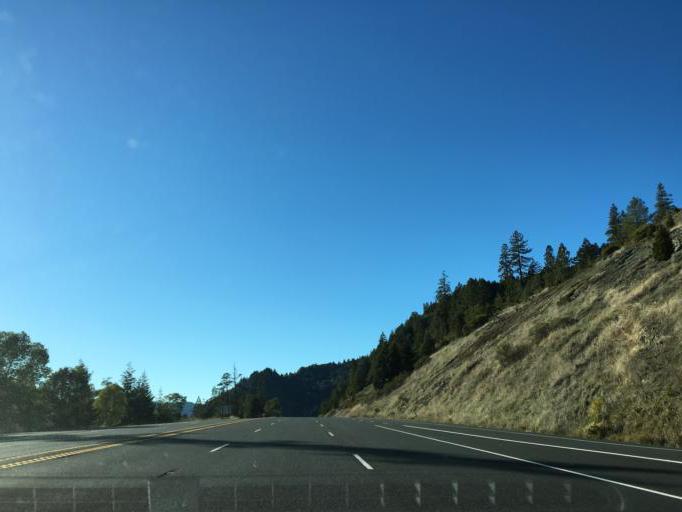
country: US
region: California
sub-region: Mendocino County
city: Laytonville
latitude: 39.8345
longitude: -123.6345
